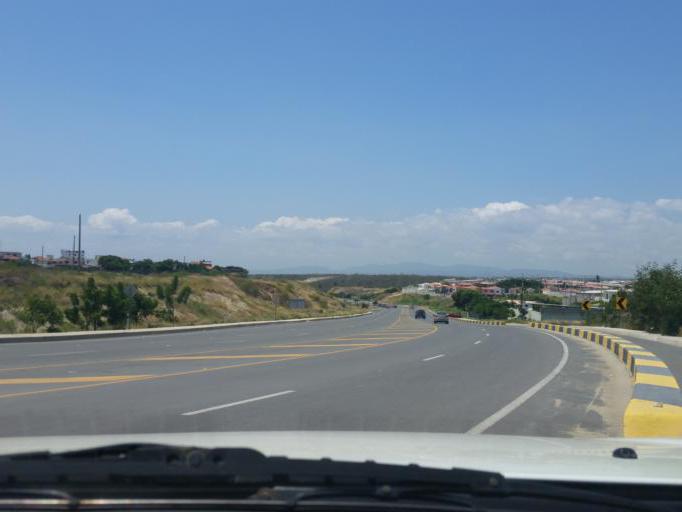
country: EC
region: Manabi
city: Manta
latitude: -0.9597
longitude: -80.7580
